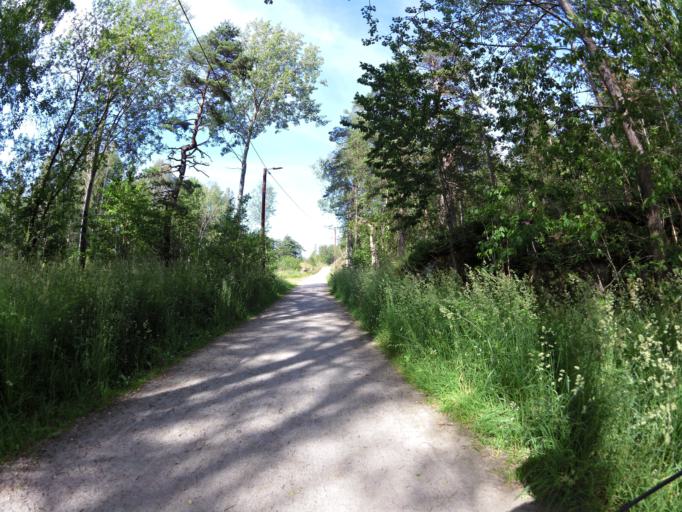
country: NO
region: Ostfold
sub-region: Fredrikstad
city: Fredrikstad
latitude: 59.2273
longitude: 10.9441
